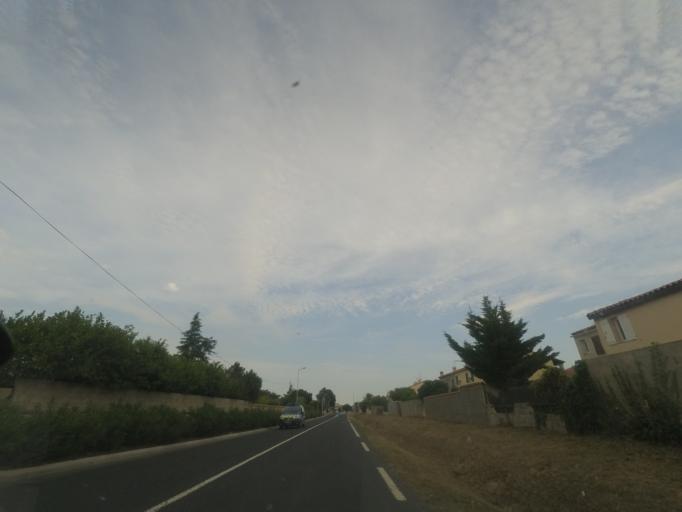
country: FR
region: Languedoc-Roussillon
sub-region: Departement des Pyrenees-Orientales
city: Le Soler
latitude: 42.6812
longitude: 2.7822
